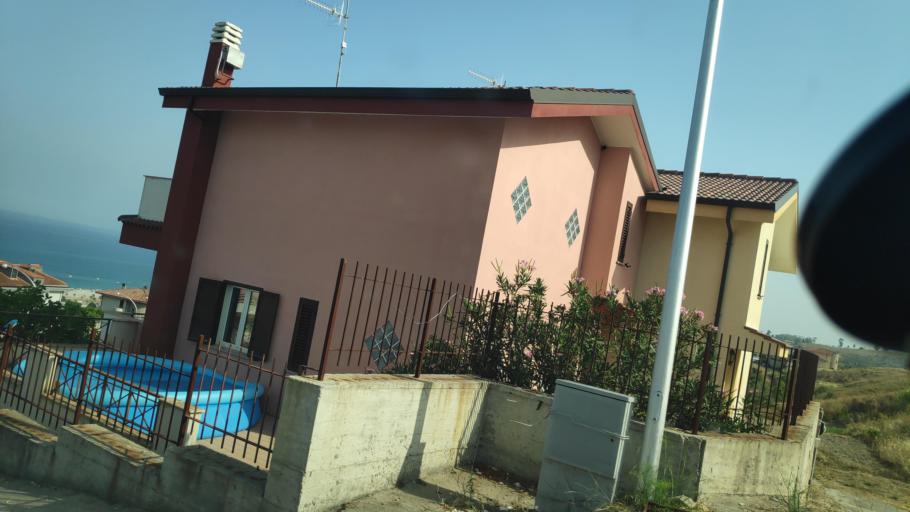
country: IT
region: Calabria
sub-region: Provincia di Catanzaro
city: Santa Caterina dello Ionio Marina
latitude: 38.5329
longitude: 16.5663
